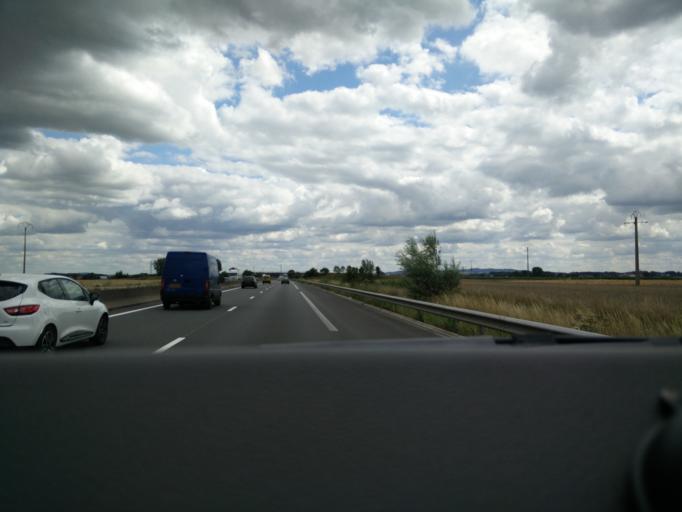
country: FR
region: Nord-Pas-de-Calais
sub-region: Departement du Nord
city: Quaedypre
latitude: 50.9233
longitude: 2.4753
